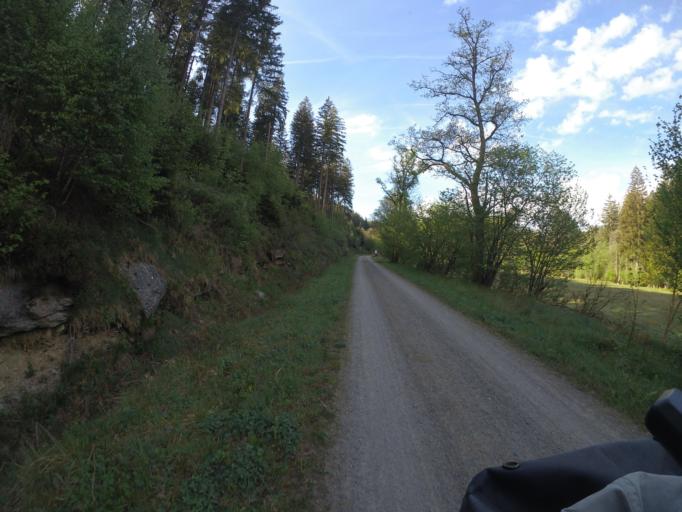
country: DE
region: North Rhine-Westphalia
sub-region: Regierungsbezirk Koln
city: Monschau
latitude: 50.5417
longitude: 6.2033
